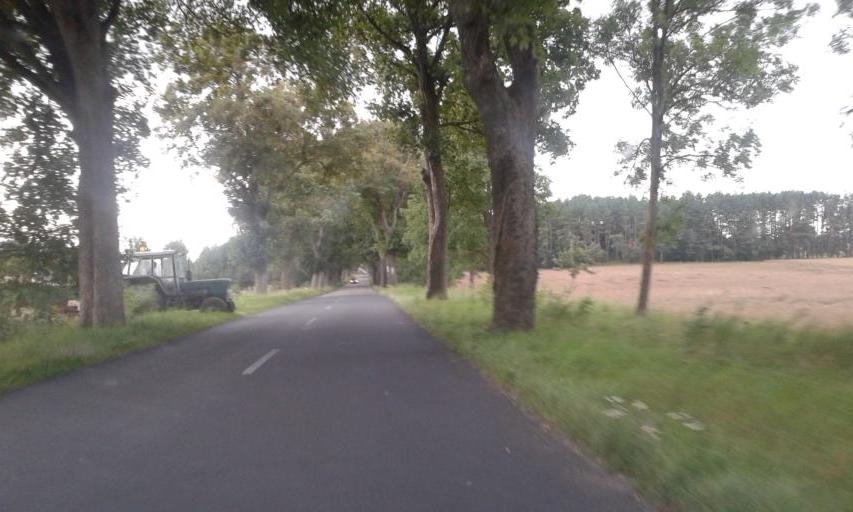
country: PL
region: West Pomeranian Voivodeship
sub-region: Powiat szczecinecki
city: Barwice
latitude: 53.7515
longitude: 16.3162
